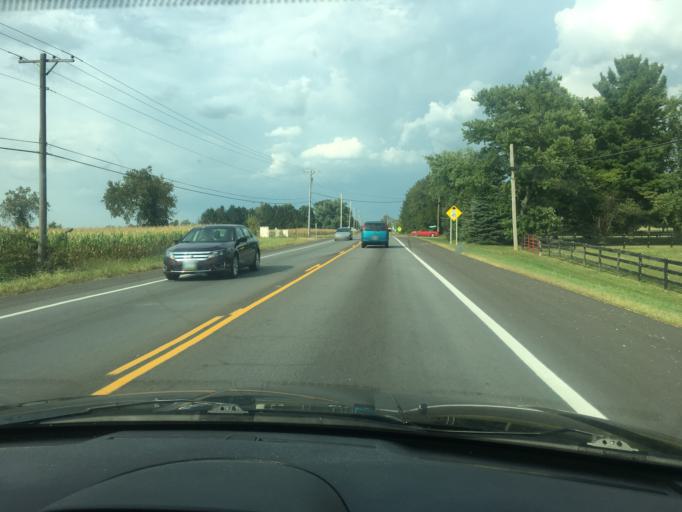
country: US
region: Ohio
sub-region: Champaign County
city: Urbana
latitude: 40.0822
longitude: -83.7614
